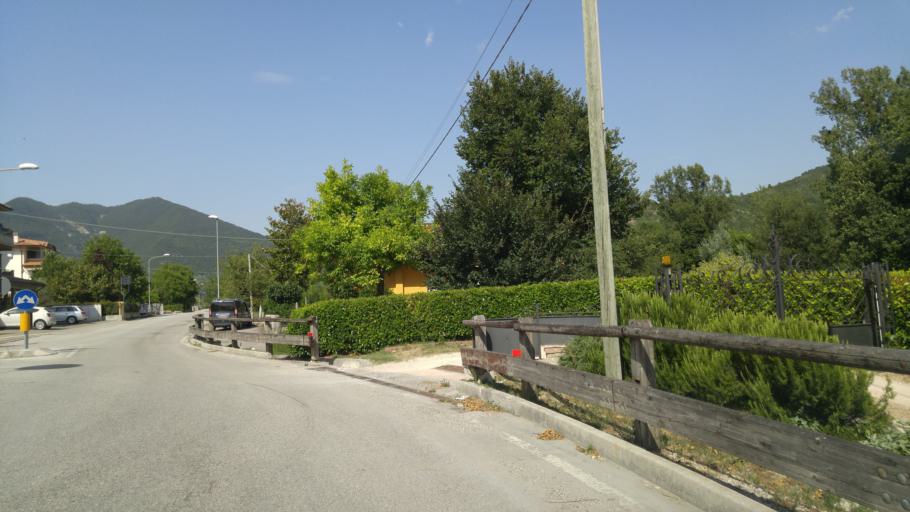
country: IT
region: The Marches
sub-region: Provincia di Pesaro e Urbino
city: Acqualagna
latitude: 43.6230
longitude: 12.6769
